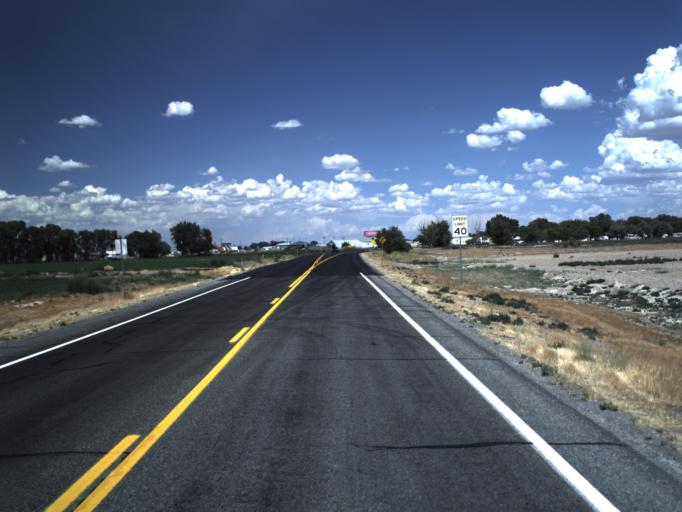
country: US
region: Utah
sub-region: Millard County
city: Delta
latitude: 39.3477
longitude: -112.5986
